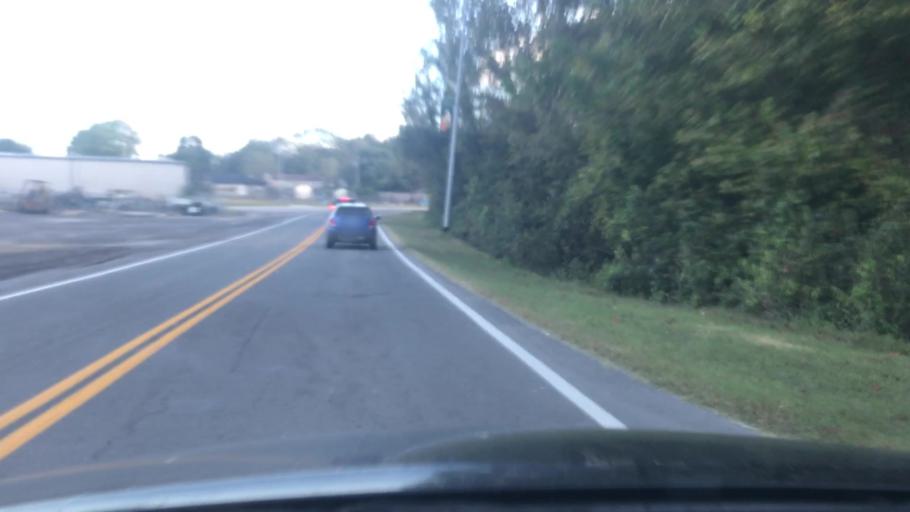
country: US
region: Tennessee
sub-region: Cheatham County
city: Ashland City
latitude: 36.2639
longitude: -87.0623
